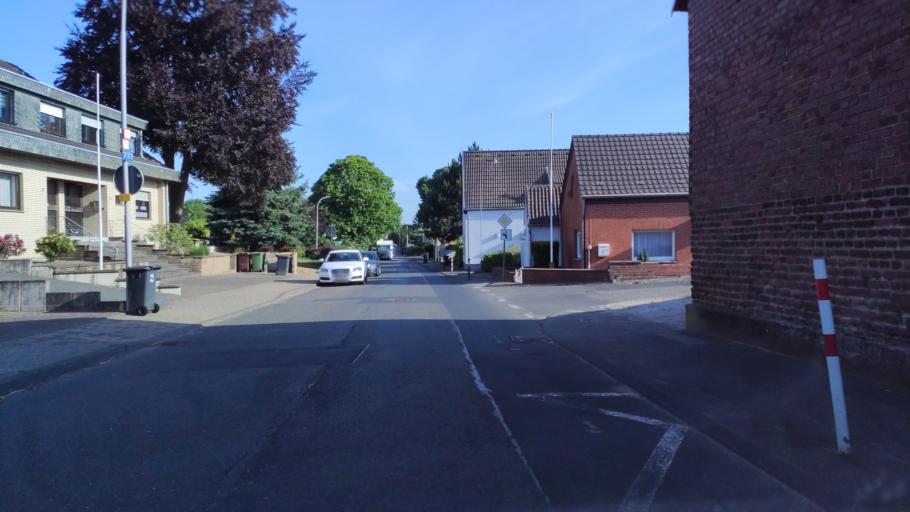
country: DE
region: North Rhine-Westphalia
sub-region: Regierungsbezirk Dusseldorf
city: Neubrueck
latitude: 51.1093
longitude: 6.7170
